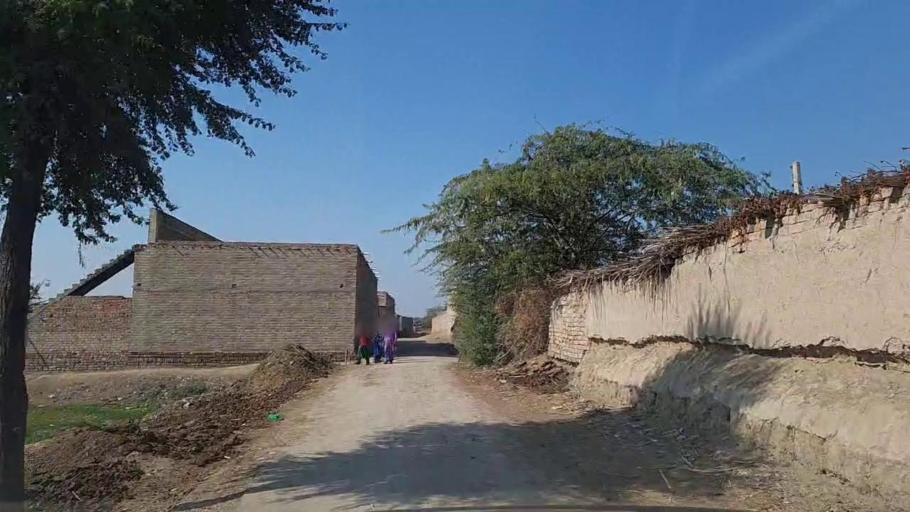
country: PK
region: Sindh
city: Nawabshah
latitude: 26.2904
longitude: 68.3784
